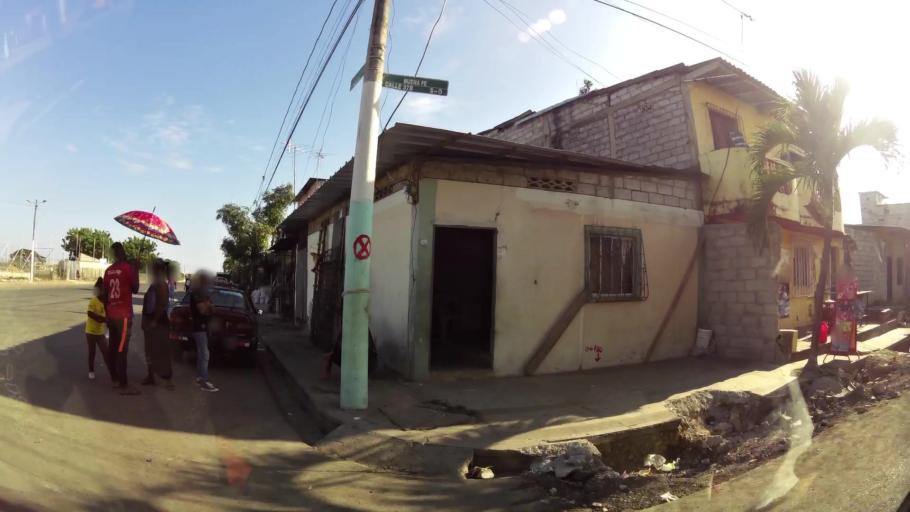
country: EC
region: Guayas
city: Guayaquil
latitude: -2.2224
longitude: -79.9173
